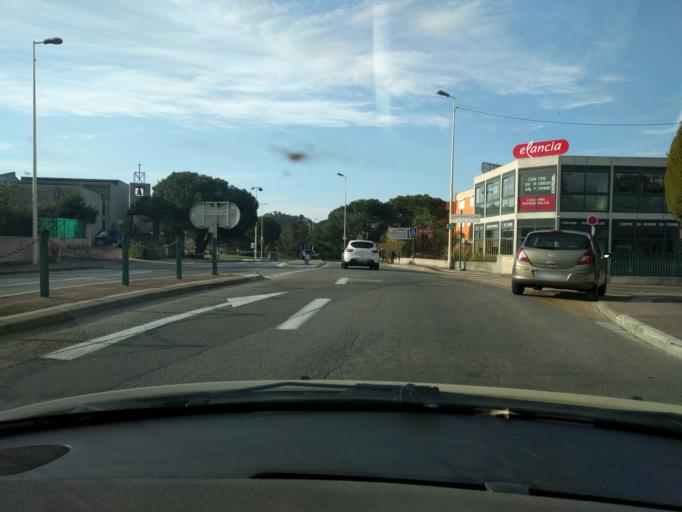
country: FR
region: Provence-Alpes-Cote d'Azur
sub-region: Departement des Alpes-Maritimes
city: Cannes
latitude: 43.5684
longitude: 6.9810
